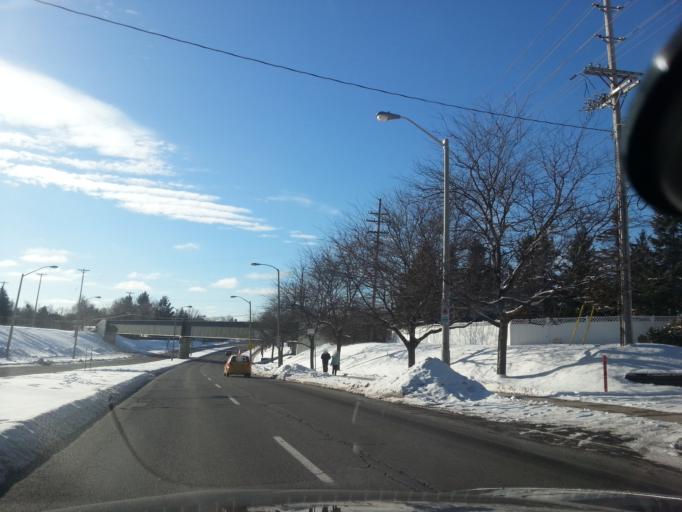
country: CA
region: Ontario
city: Ottawa
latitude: 45.3635
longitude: -75.6801
